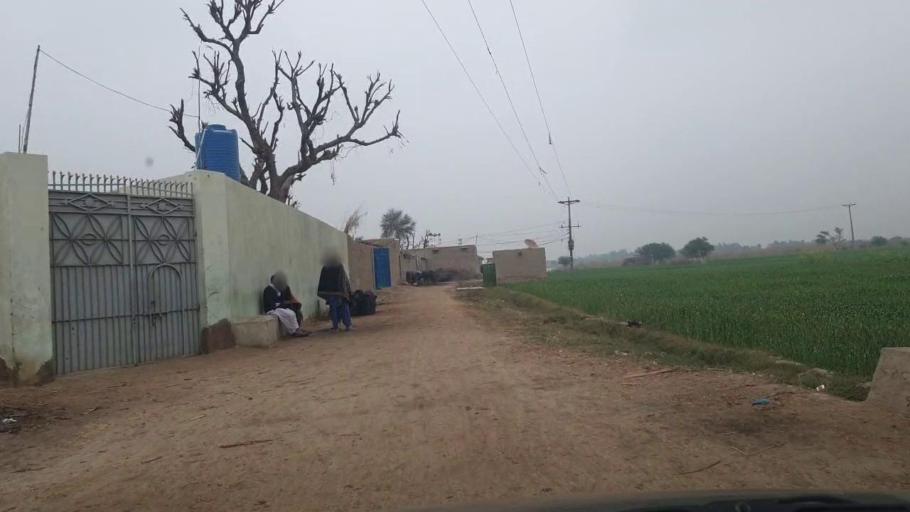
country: PK
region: Sindh
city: Tando Adam
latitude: 25.8514
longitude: 68.6760
